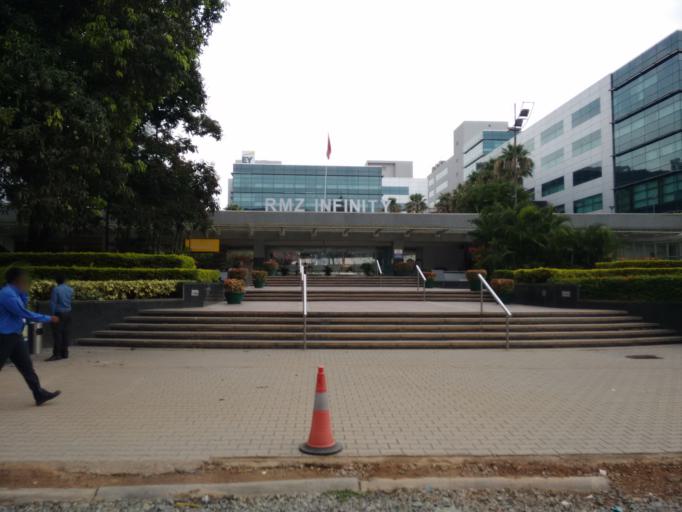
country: IN
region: Karnataka
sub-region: Bangalore Urban
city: Bangalore
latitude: 12.9933
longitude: 77.6611
